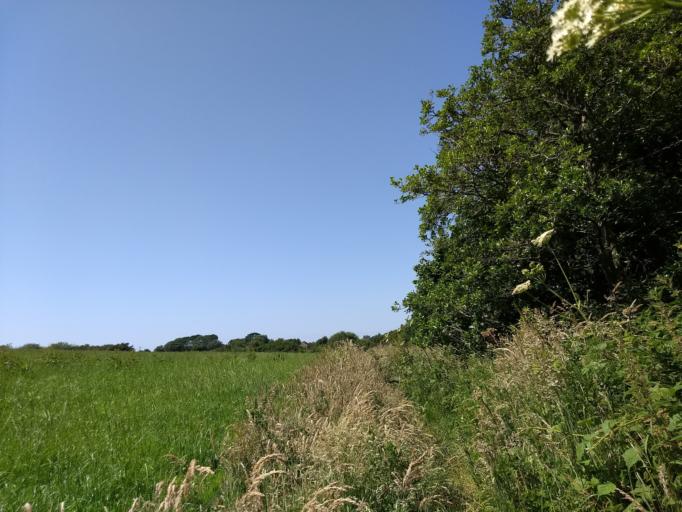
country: GB
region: England
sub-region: Isle of Wight
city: Shalfleet
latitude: 50.6948
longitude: -1.4146
